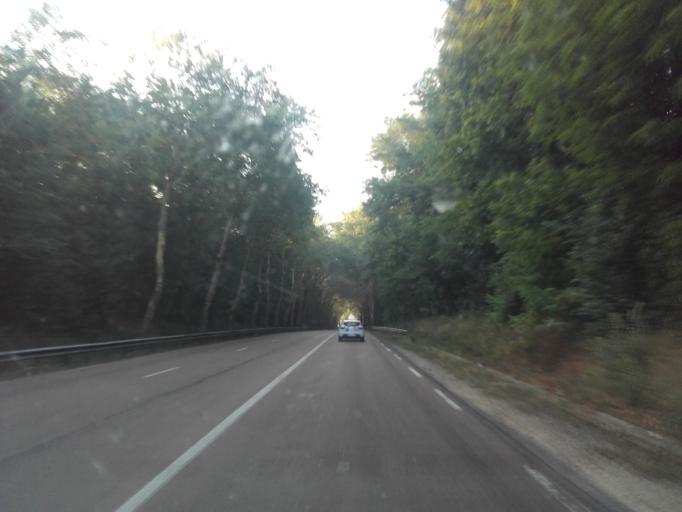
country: FR
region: Bourgogne
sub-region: Departement de l'Yonne
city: Auxerre
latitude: 47.8298
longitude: 3.5539
